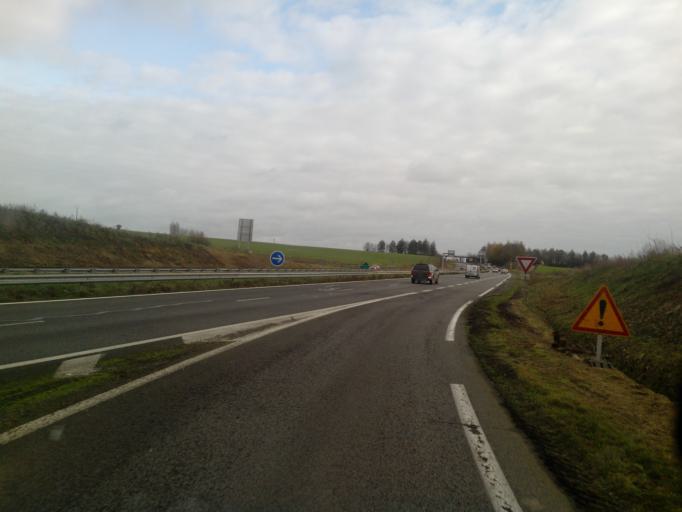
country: FR
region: Brittany
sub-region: Departement d'Ille-et-Vilaine
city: Montauban-de-Bretagne
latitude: 48.2089
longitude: -2.0734
